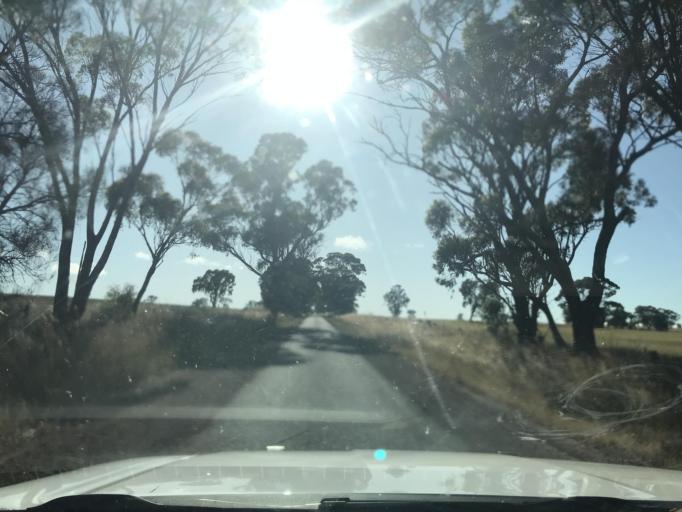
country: AU
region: Victoria
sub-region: Horsham
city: Horsham
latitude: -36.6974
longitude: 141.5984
